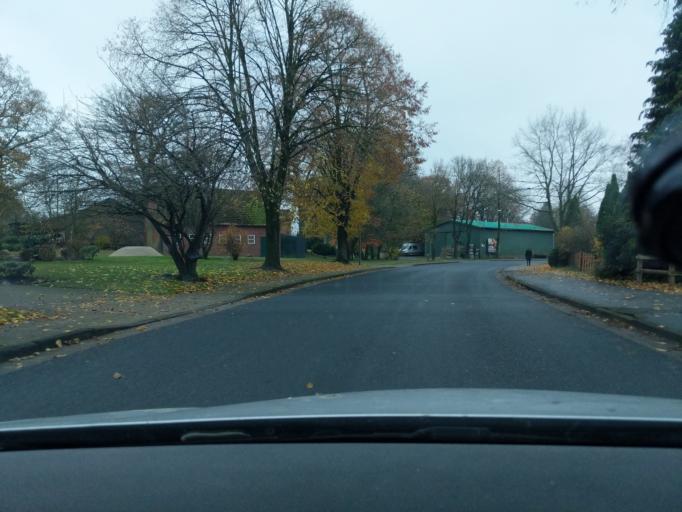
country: DE
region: Lower Saxony
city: Klein Meckelsen
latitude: 53.3478
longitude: 9.4001
